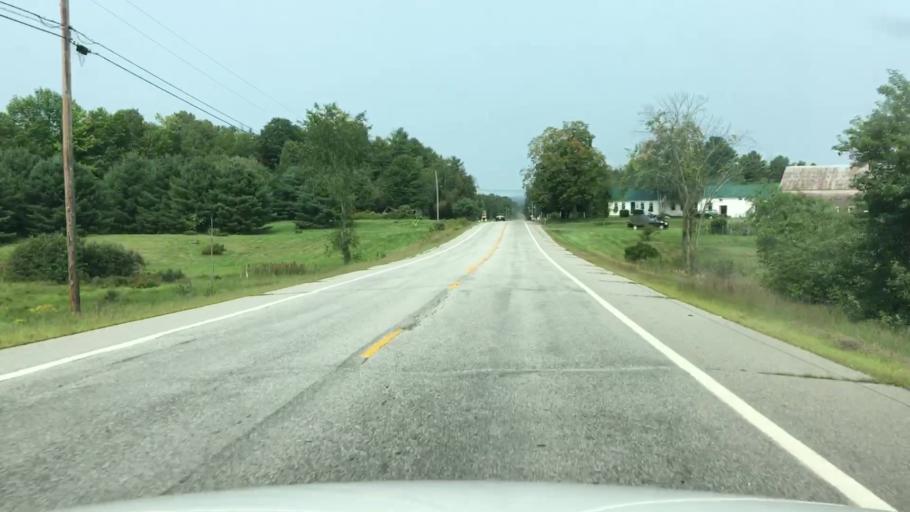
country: US
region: Maine
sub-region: Kennebec County
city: Wayne
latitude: 44.4002
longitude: -70.1247
